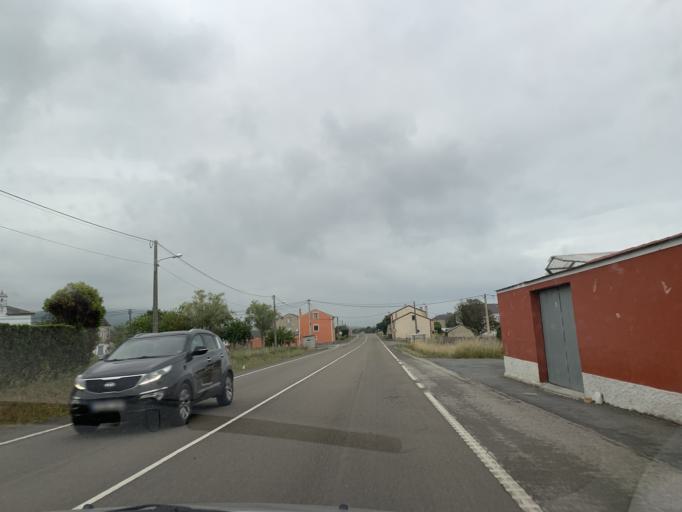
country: ES
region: Galicia
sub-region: Provincia de Lugo
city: Ribadeo
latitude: 43.5458
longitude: -7.0903
